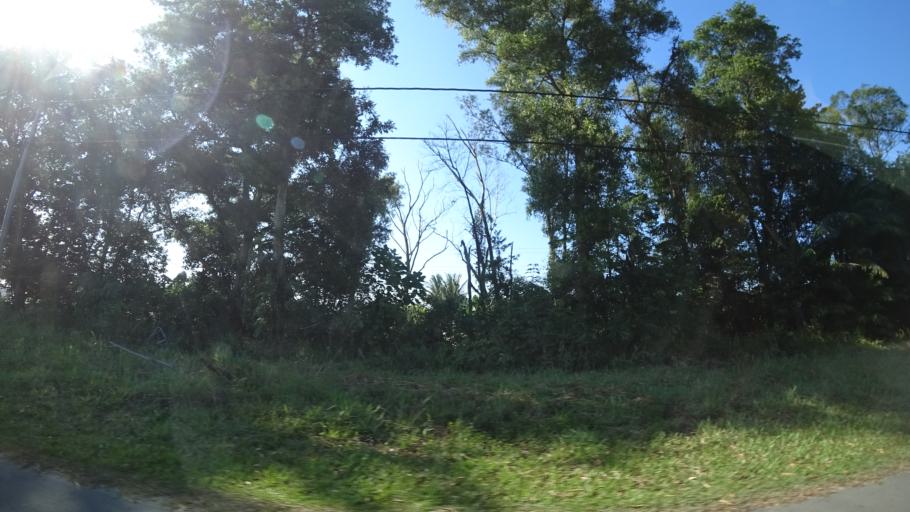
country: BN
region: Tutong
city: Tutong
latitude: 4.6991
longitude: 114.5208
